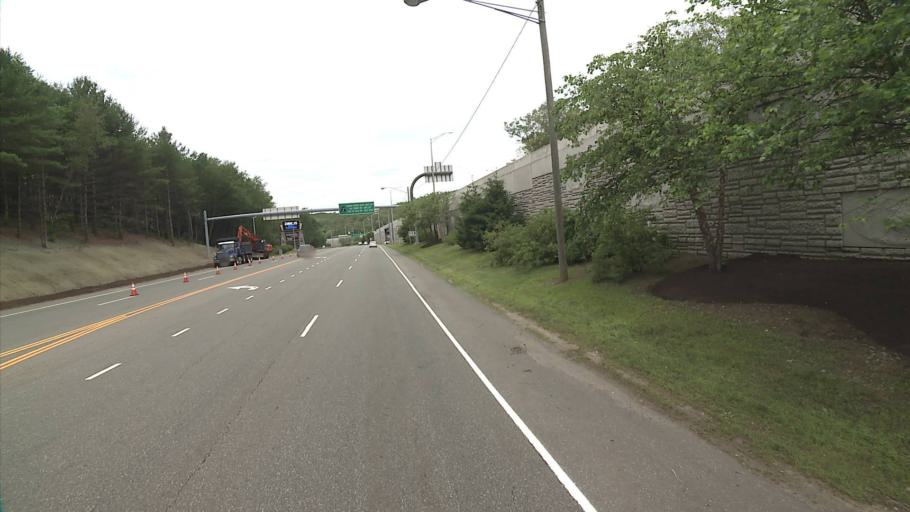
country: US
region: Connecticut
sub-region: New London County
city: Preston City
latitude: 41.4742
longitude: -71.9554
